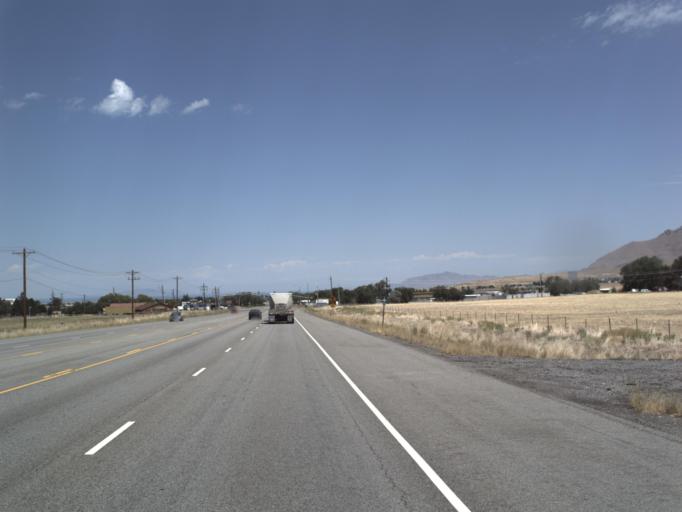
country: US
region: Utah
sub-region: Tooele County
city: Erda
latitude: 40.5949
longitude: -112.2940
